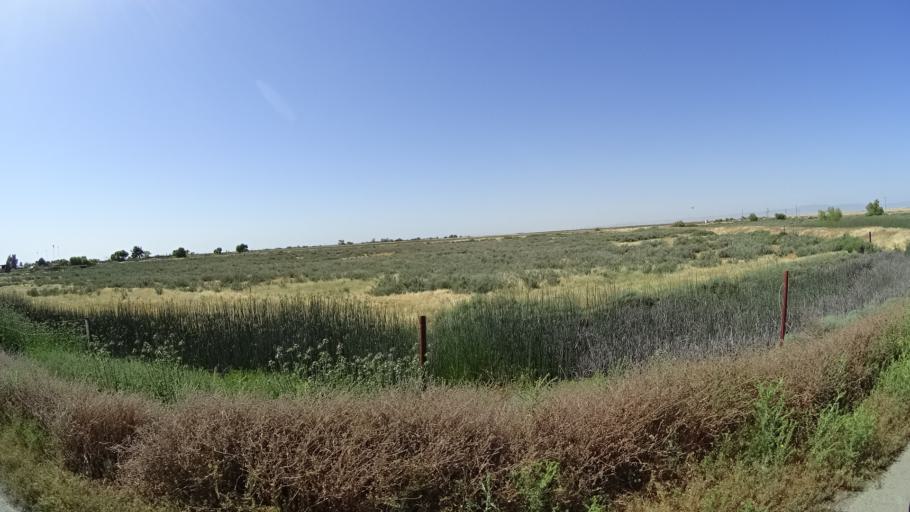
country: US
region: California
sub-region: Kings County
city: Lemoore Station
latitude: 36.2505
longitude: -119.8593
